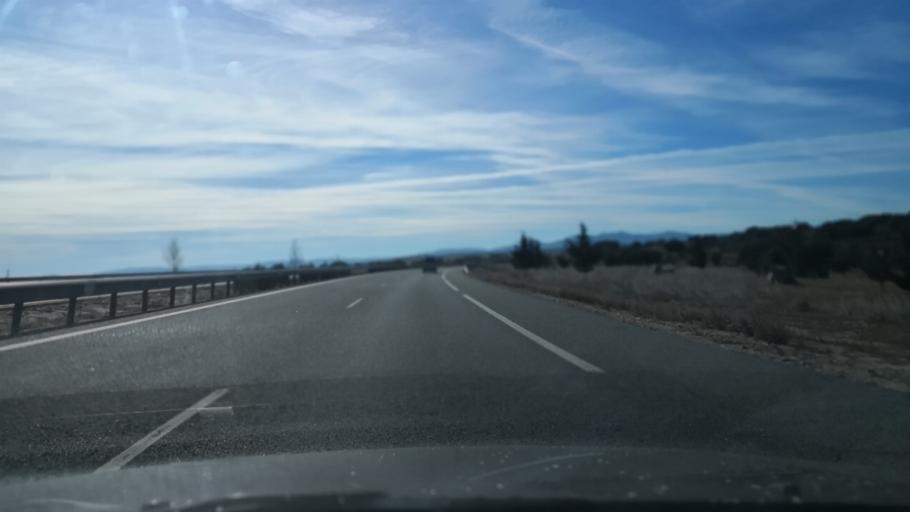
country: ES
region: Castille and Leon
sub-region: Provincia de Avila
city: Cardenosa
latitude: 40.7251
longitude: -4.7429
